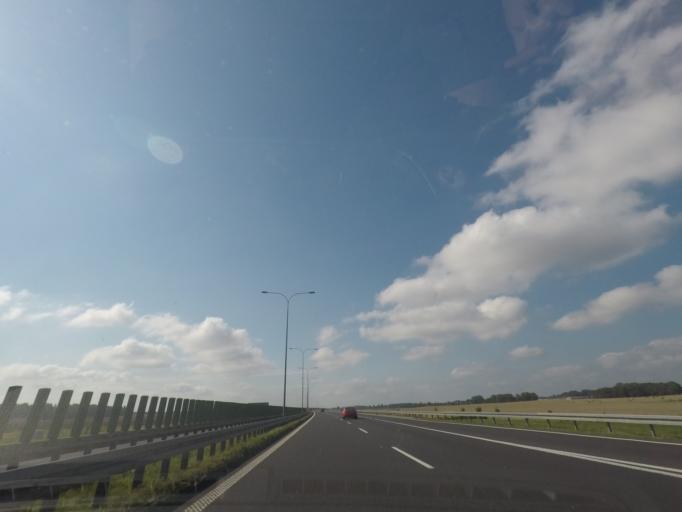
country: PL
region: Pomeranian Voivodeship
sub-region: Powiat starogardzki
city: Smetowo Graniczne
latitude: 53.7326
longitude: 18.6284
